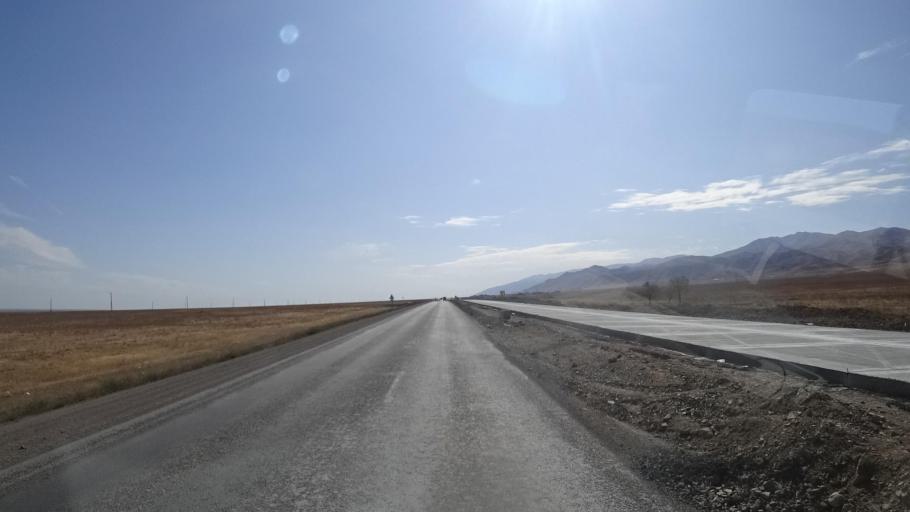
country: KG
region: Chuy
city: Ivanovka
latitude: 43.3981
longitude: 75.1208
